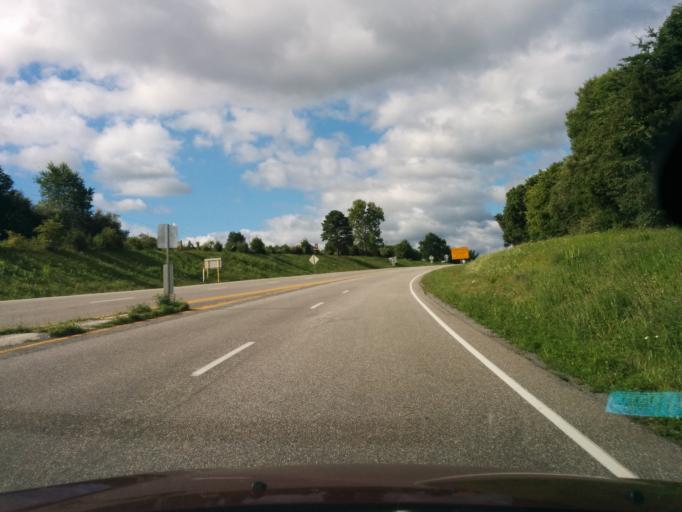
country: US
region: Virginia
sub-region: Rockbridge County
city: Glasgow
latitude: 37.6679
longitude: -79.5066
